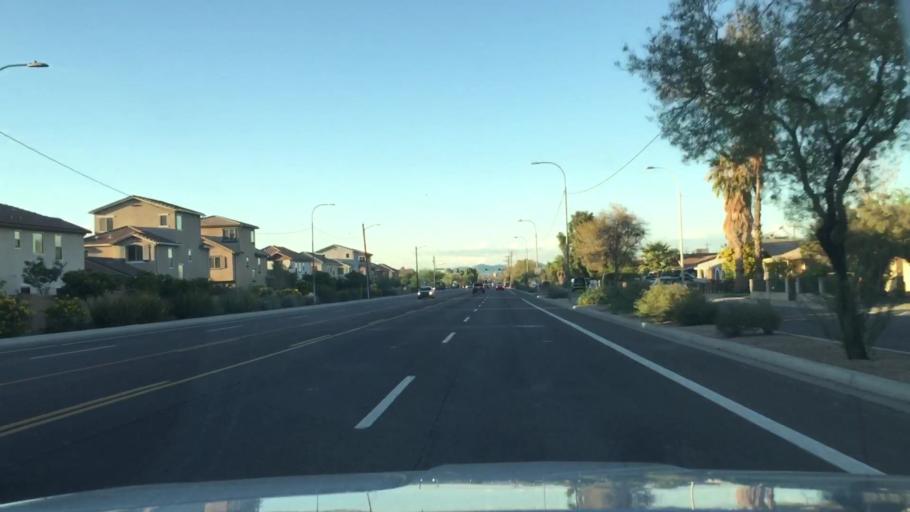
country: US
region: Arizona
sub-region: Maricopa County
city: Phoenix
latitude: 33.3827
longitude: -112.0819
